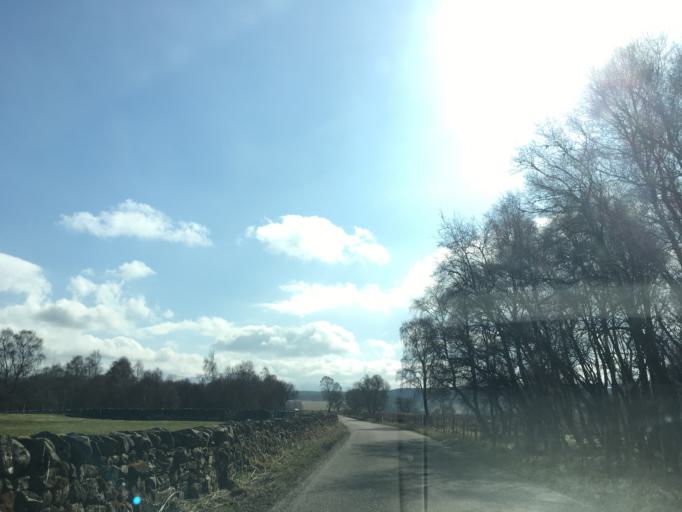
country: GB
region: Scotland
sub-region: Highland
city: Kingussie
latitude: 57.0720
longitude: -4.0167
